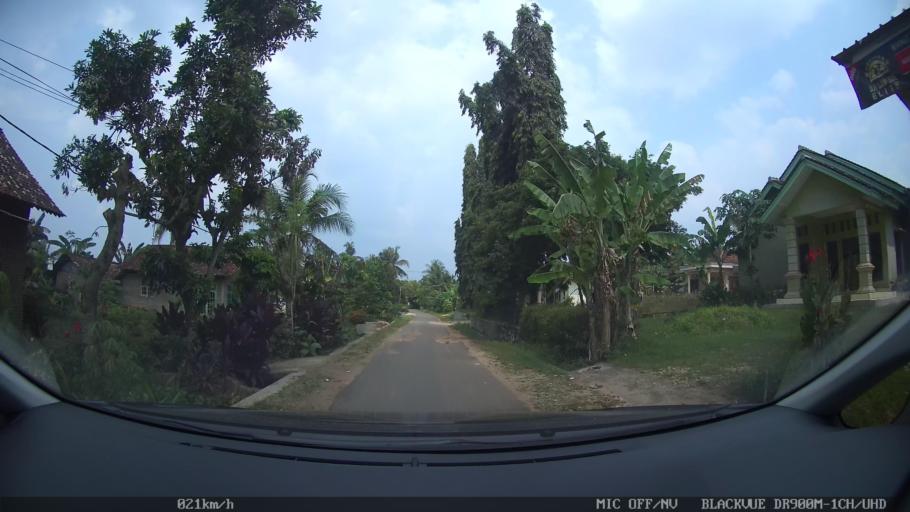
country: ID
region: Lampung
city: Gadingrejo
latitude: -5.3650
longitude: 105.0616
